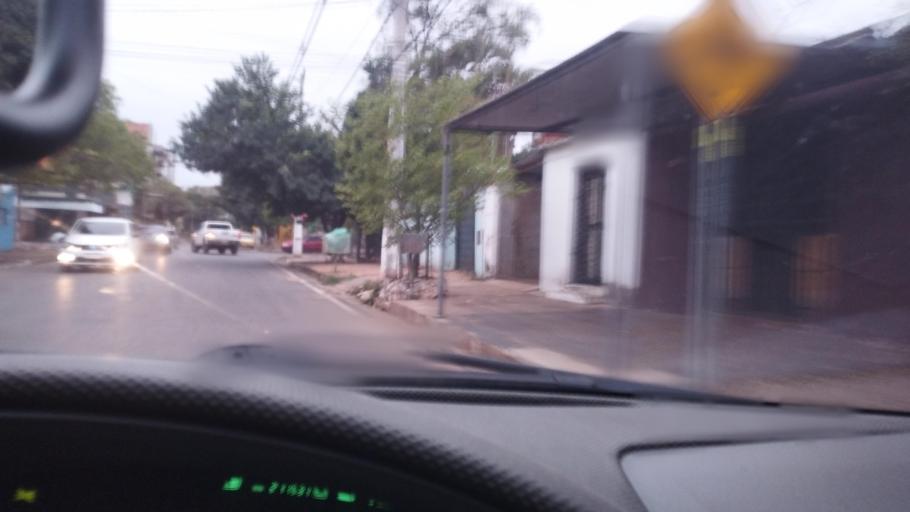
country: PY
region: Central
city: Fernando de la Mora
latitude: -25.3000
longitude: -57.5292
